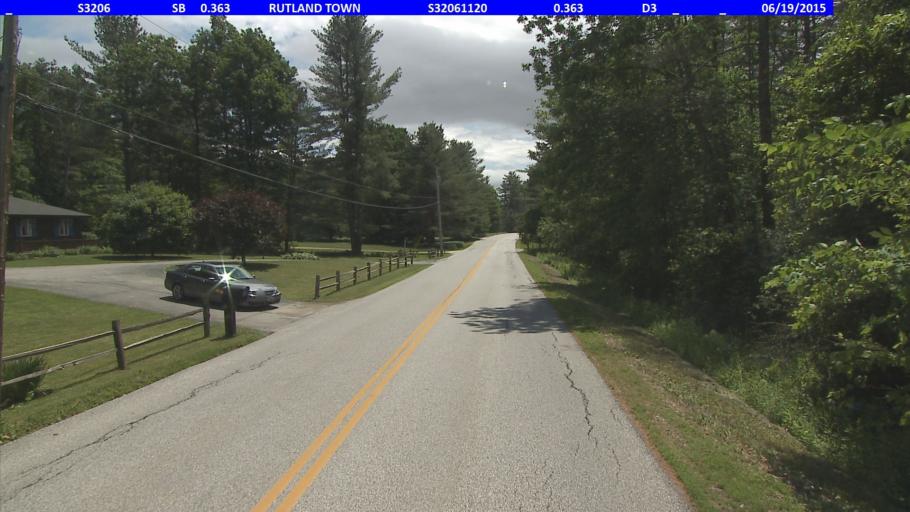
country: US
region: Vermont
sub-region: Rutland County
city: Rutland
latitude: 43.6349
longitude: -72.9898
